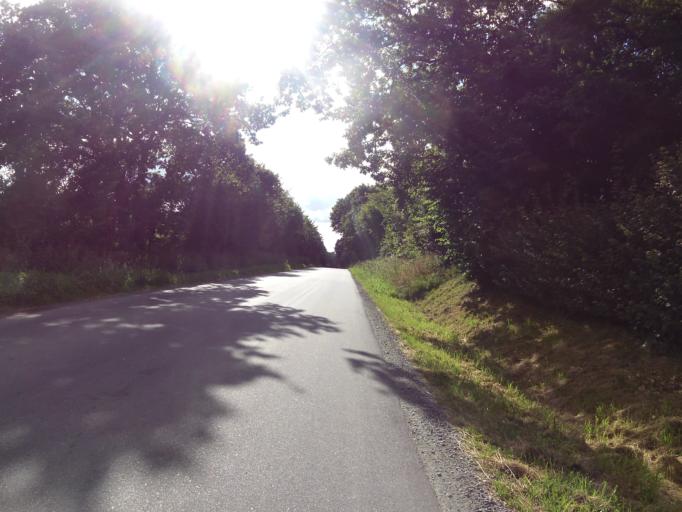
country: DK
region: South Denmark
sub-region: Haderslev Kommune
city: Haderslev
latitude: 55.2067
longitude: 9.4182
